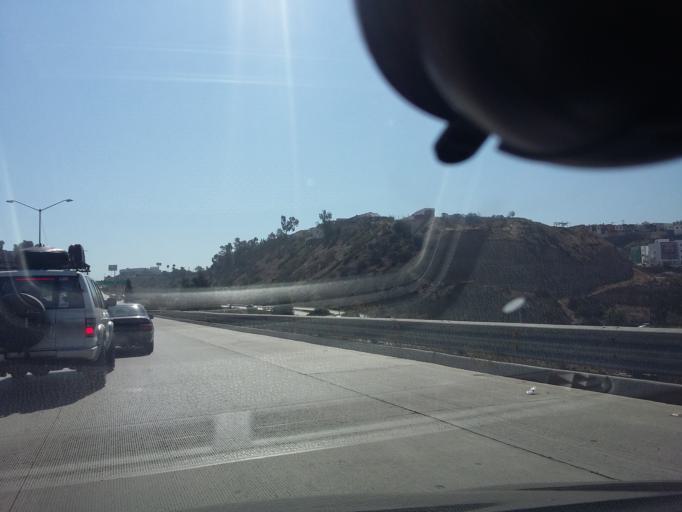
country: US
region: California
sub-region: San Diego County
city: Imperial Beach
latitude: 32.5324
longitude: -117.0850
